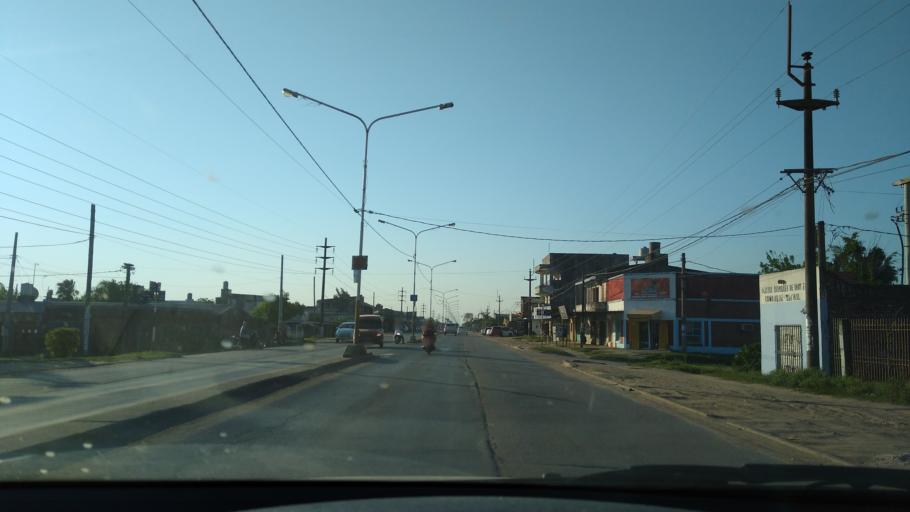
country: AR
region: Chaco
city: Barranqueras
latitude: -27.4914
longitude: -58.9554
